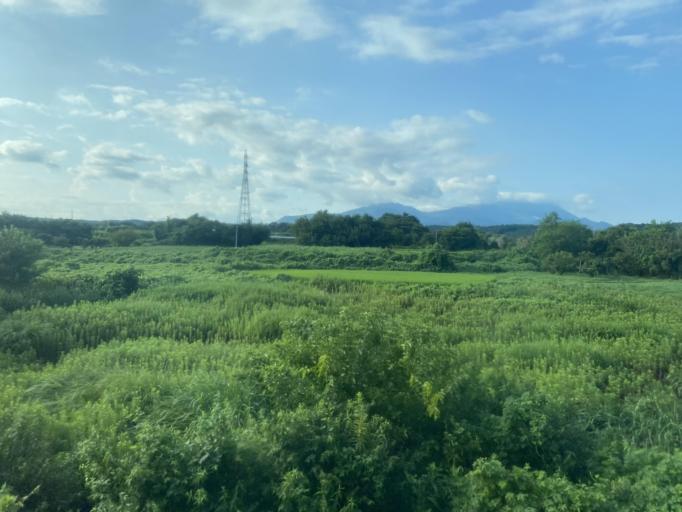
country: JP
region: Tottori
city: Yonago
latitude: 35.5179
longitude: 133.5621
